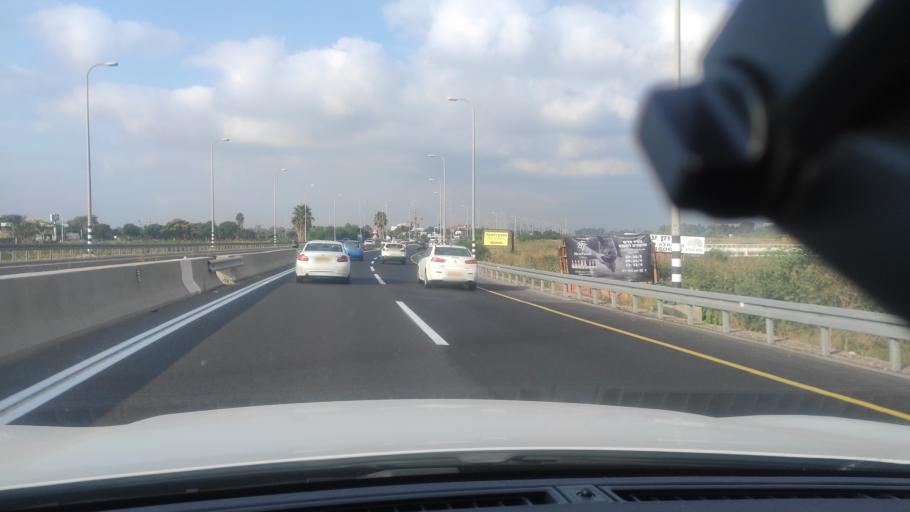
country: IL
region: Central District
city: Hod HaSharon
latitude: 32.1396
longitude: 34.9164
